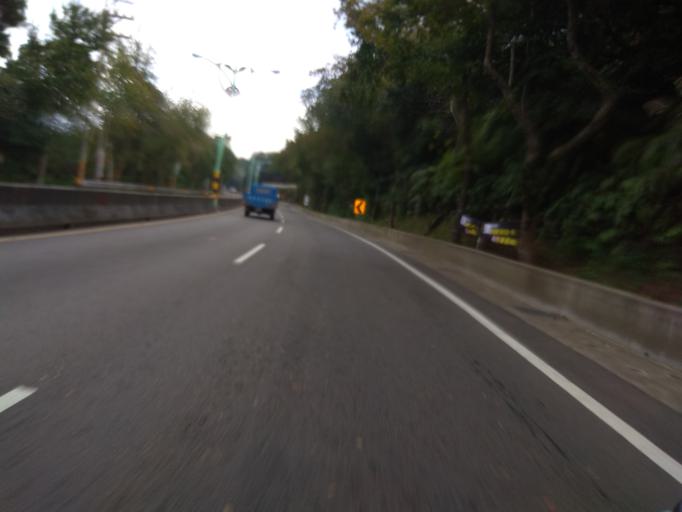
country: TW
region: Taiwan
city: Daxi
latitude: 24.8514
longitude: 121.2048
